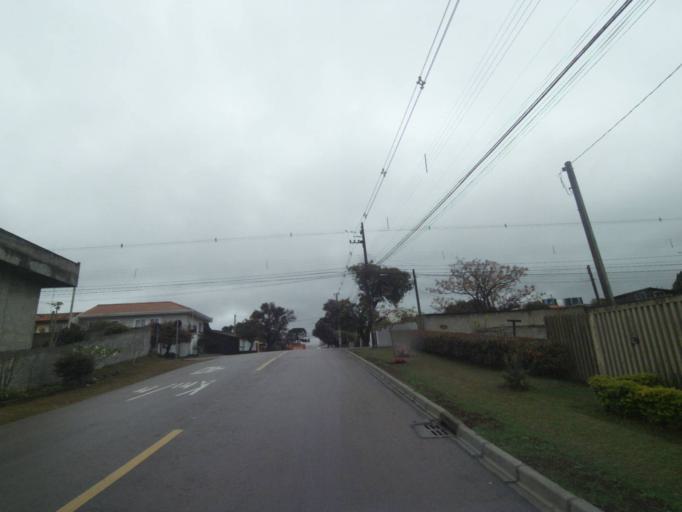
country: BR
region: Parana
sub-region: Curitiba
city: Curitiba
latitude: -25.5158
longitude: -49.3008
